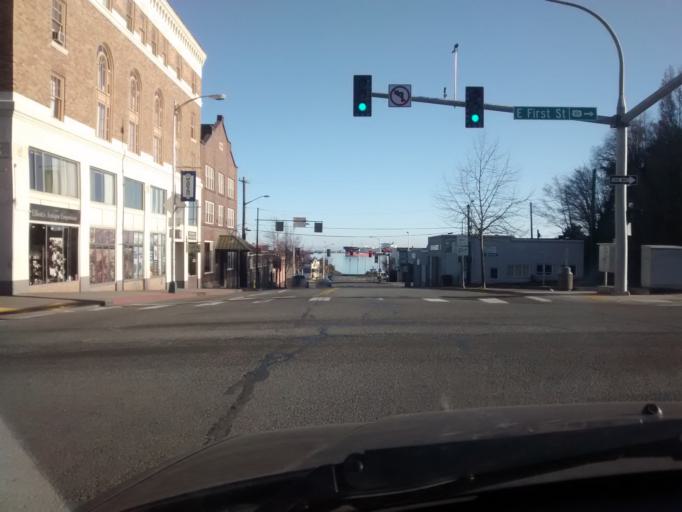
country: US
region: Washington
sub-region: Clallam County
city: Port Angeles
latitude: 48.1182
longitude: -123.4318
